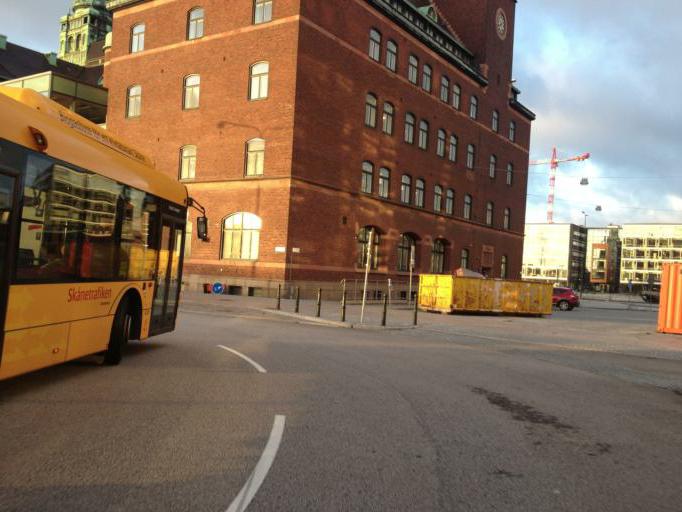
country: SE
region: Skane
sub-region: Malmo
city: Malmoe
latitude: 55.6105
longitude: 12.9994
